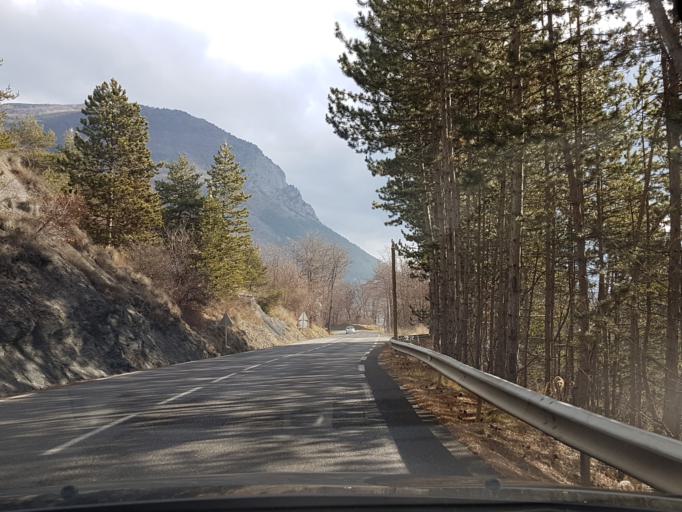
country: FR
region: Provence-Alpes-Cote d'Azur
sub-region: Departement des Hautes-Alpes
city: Tallard
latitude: 44.4764
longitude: 6.1157
